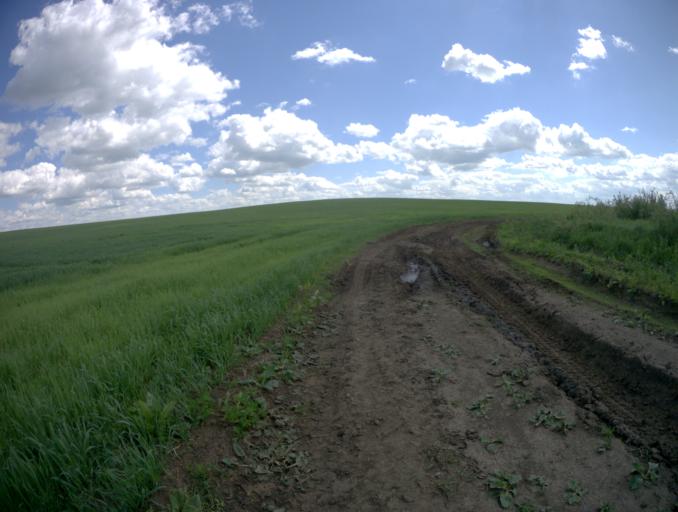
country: RU
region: Vladimir
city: Suzdal'
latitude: 56.4367
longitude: 40.2827
